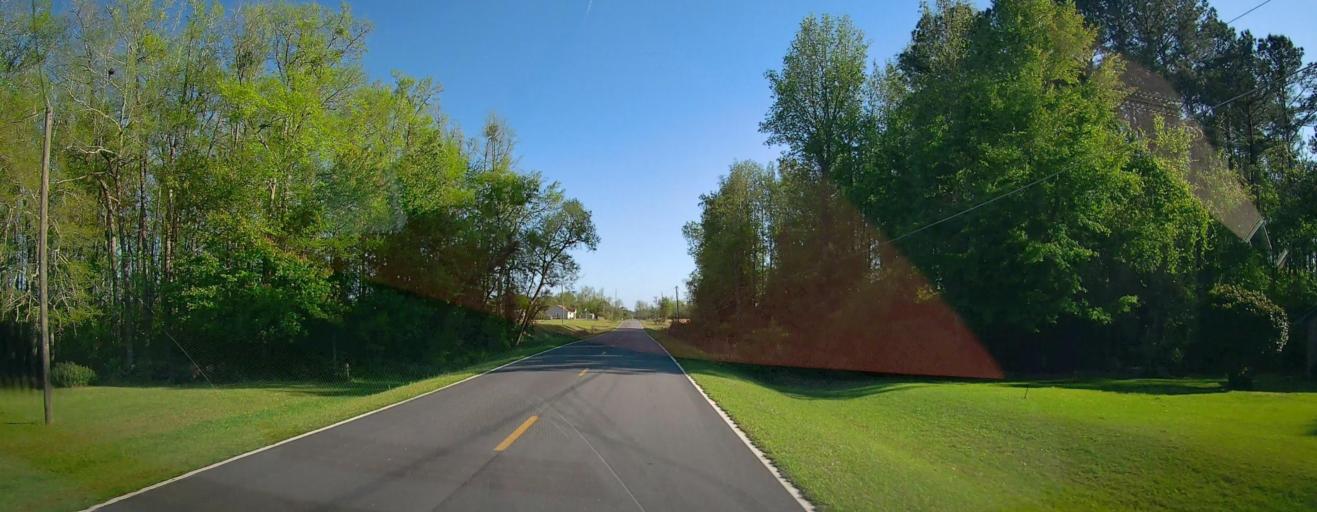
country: US
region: Georgia
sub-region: Ben Hill County
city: Fitzgerald
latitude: 31.7405
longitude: -83.2803
